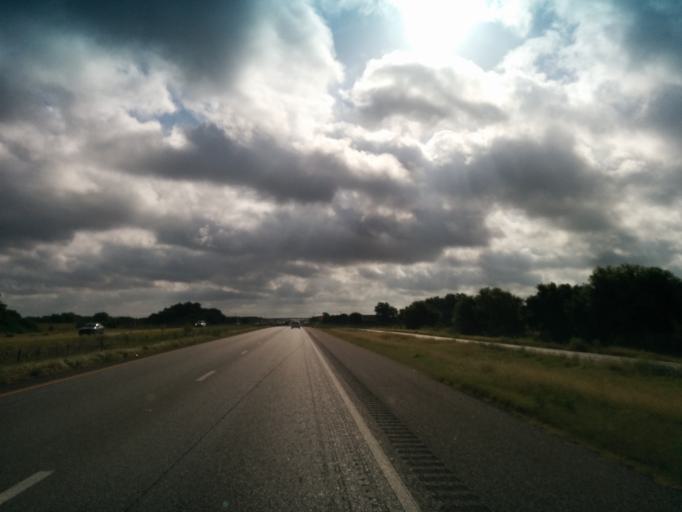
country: US
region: Texas
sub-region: Guadalupe County
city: Marion
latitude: 29.5046
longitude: -98.1767
